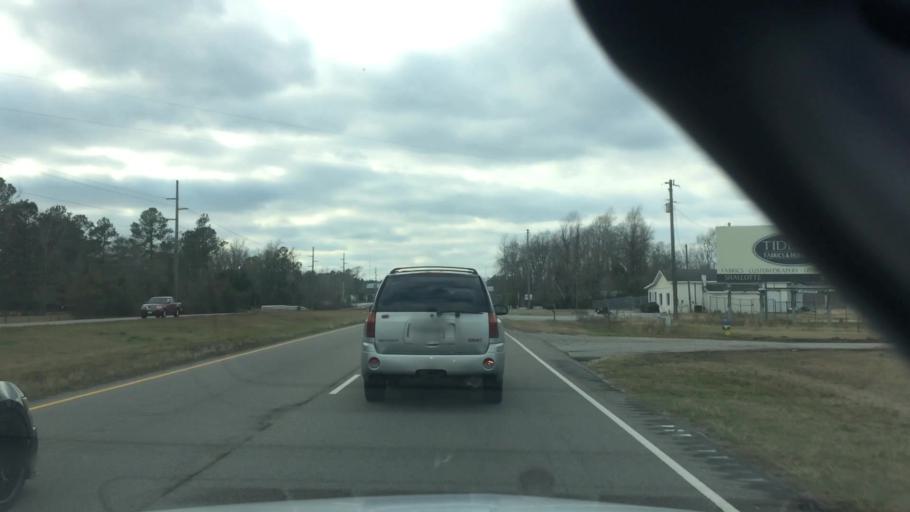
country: US
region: North Carolina
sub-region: Brunswick County
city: Shallotte
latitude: 34.0101
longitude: -78.2939
